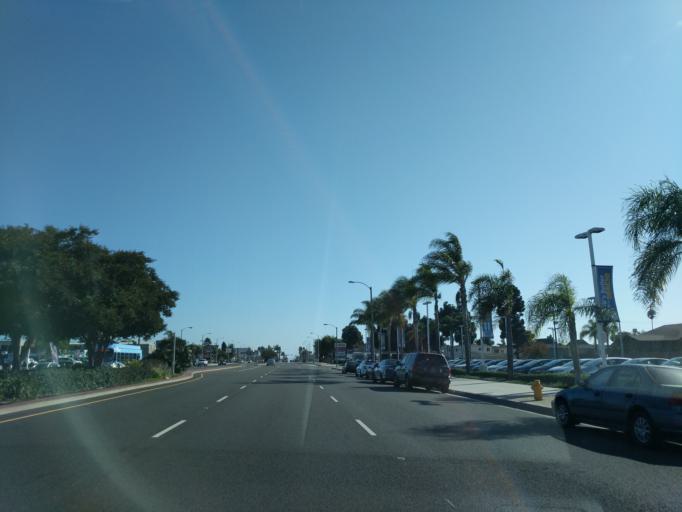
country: US
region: California
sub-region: Orange County
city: Huntington Beach
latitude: 33.6843
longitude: -117.9888
